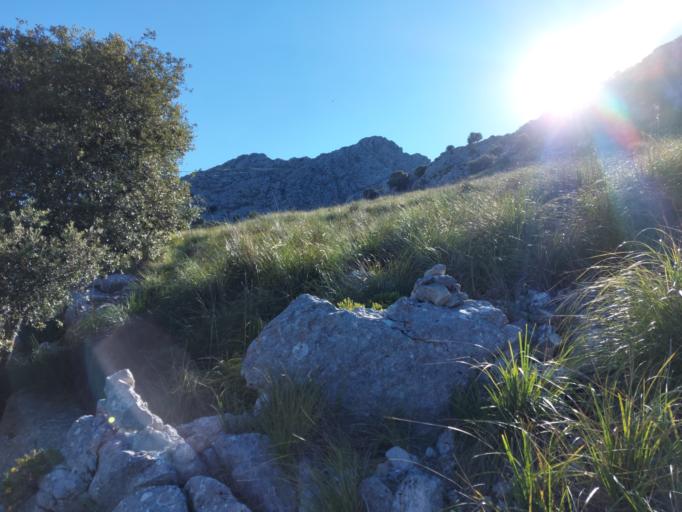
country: ES
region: Balearic Islands
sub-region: Illes Balears
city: Escorca
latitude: 39.7981
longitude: 2.8294
